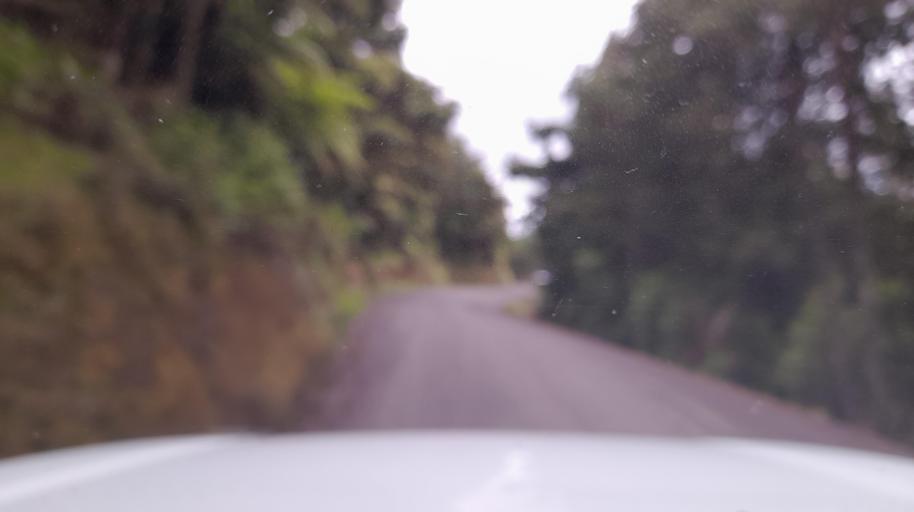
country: NZ
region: Northland
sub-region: Far North District
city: Kaitaia
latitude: -35.3200
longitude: 173.3495
